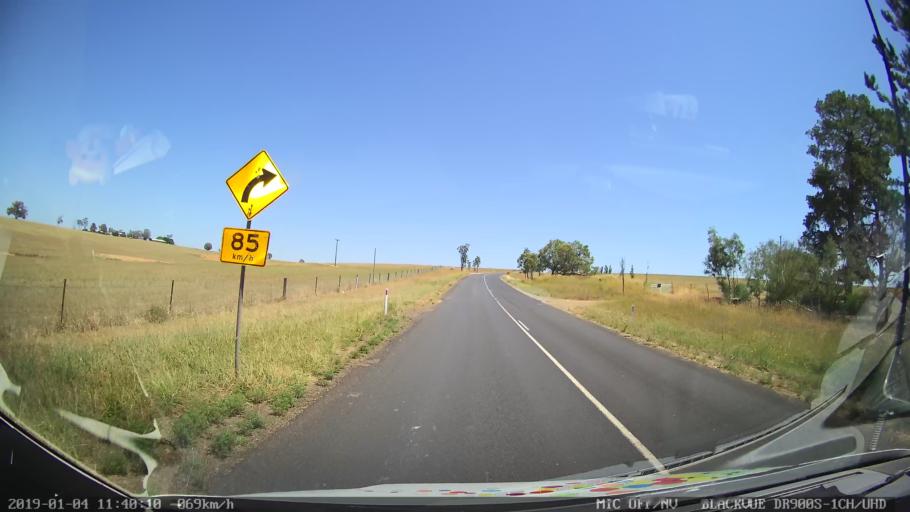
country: AU
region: New South Wales
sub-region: Cabonne
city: Molong
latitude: -33.0071
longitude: 148.7890
